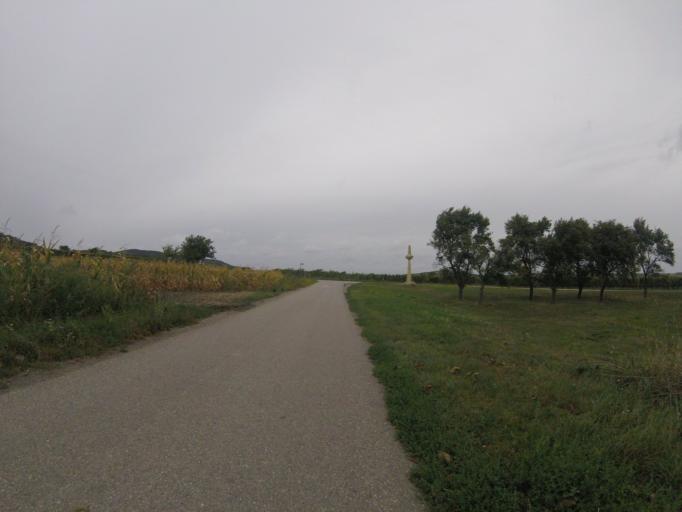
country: AT
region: Burgenland
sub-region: Politischer Bezirk Neusiedl am See
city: Winden am See
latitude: 47.9589
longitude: 16.7465
